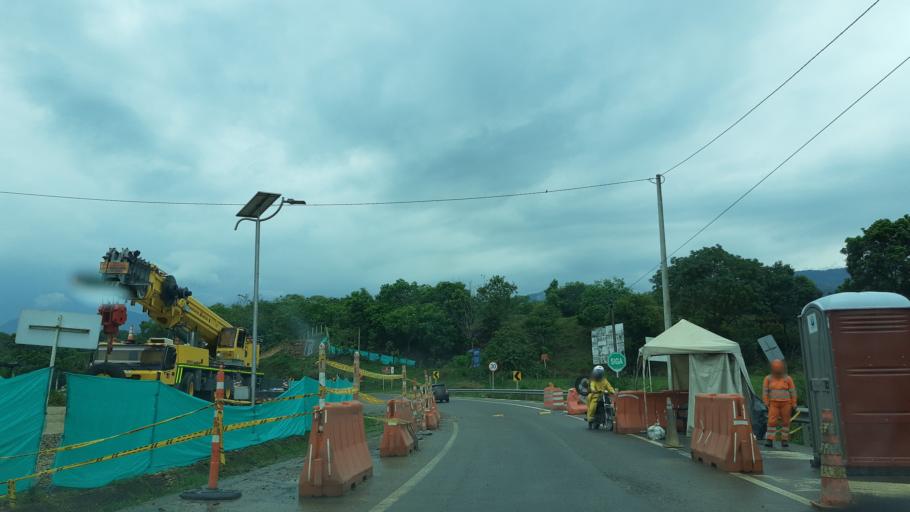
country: CO
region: Casanare
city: Monterrey
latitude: 4.8857
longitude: -72.9010
